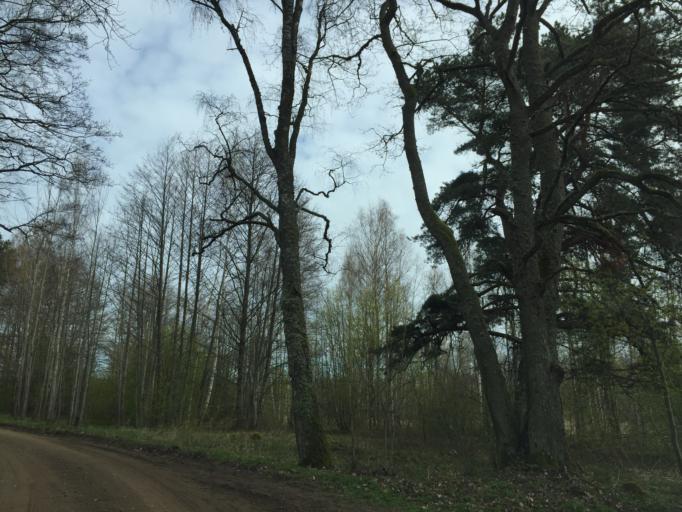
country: LV
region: Salacgrivas
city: Salacgriva
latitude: 57.5228
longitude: 24.3797
